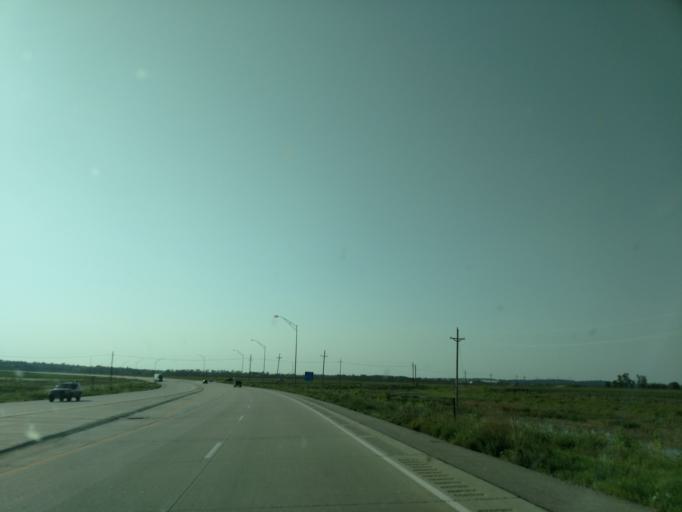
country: US
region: Nebraska
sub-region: Sarpy County
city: Offutt Air Force Base
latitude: 41.0748
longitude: -95.8886
